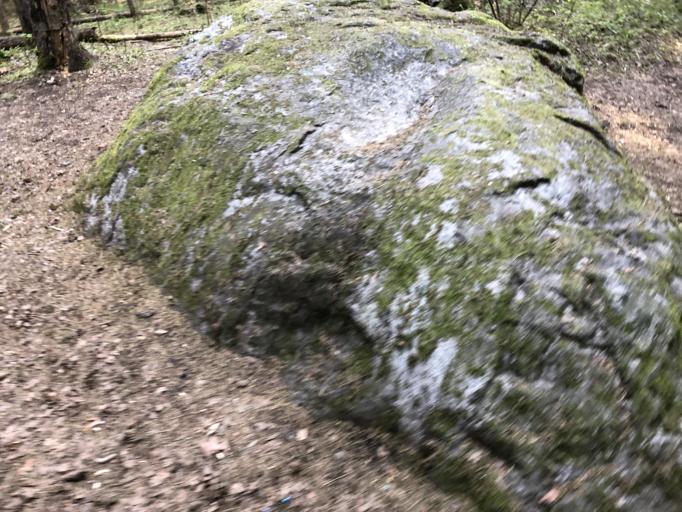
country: BY
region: Minsk
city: Zaslawye
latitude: 53.9533
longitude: 27.2657
